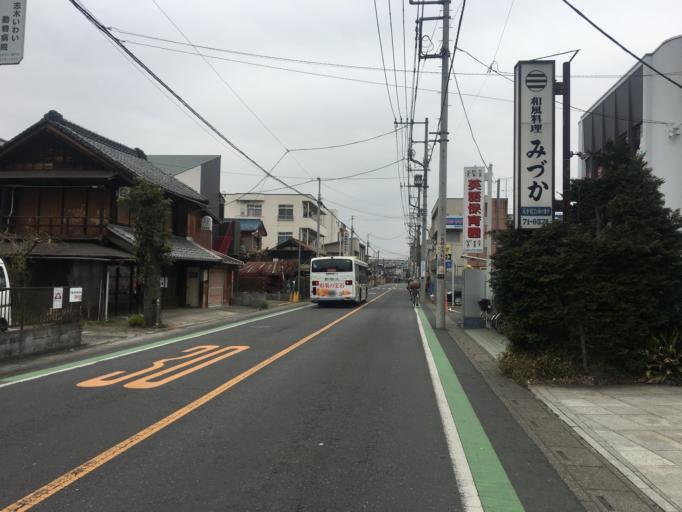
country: JP
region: Saitama
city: Shiki
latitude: 35.8270
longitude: 139.5764
